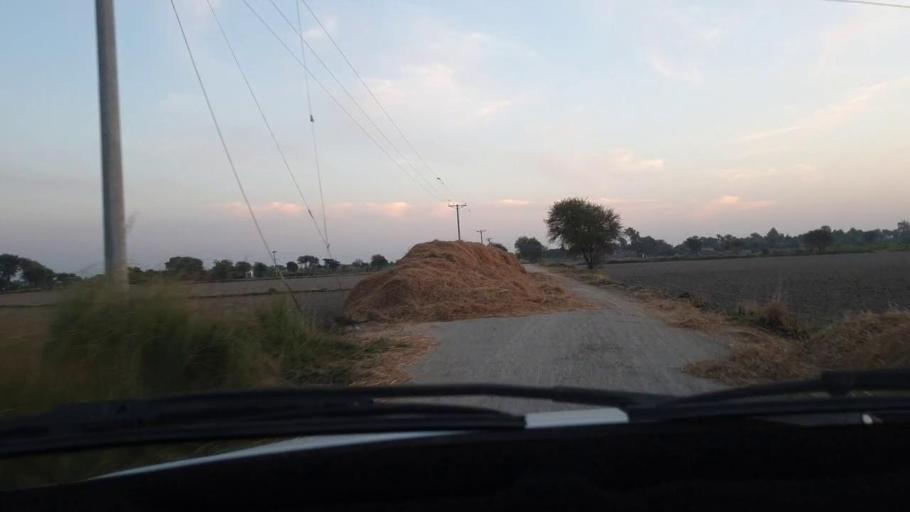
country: PK
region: Sindh
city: Tando Muhammad Khan
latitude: 25.0829
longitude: 68.3980
